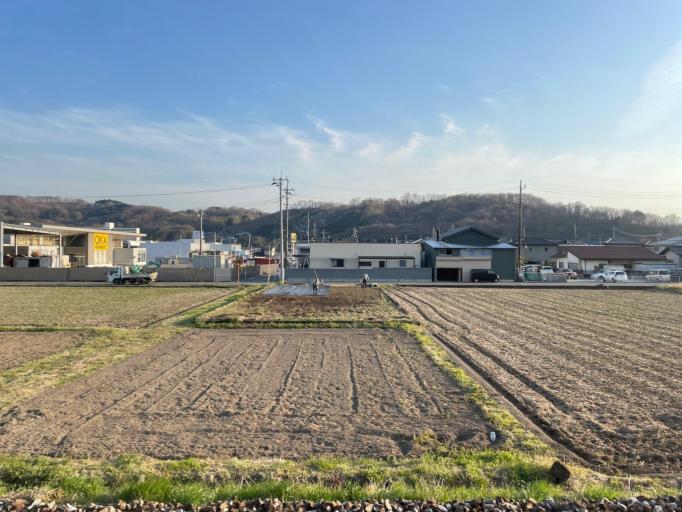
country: JP
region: Gunma
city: Annaka
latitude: 36.3380
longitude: 138.9413
